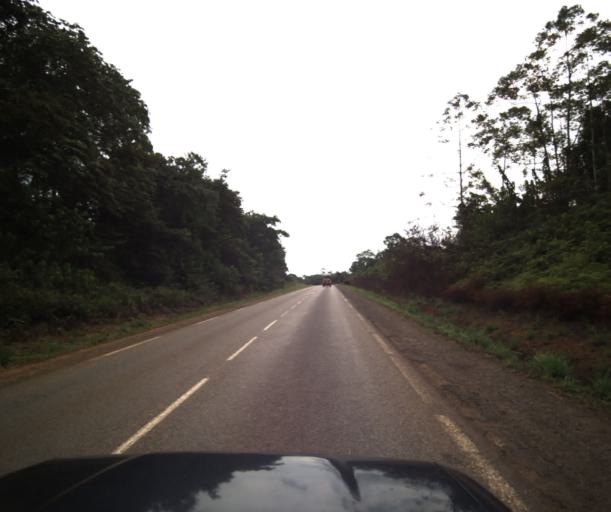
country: CM
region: Littoral
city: Edea
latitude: 3.8329
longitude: 10.4056
